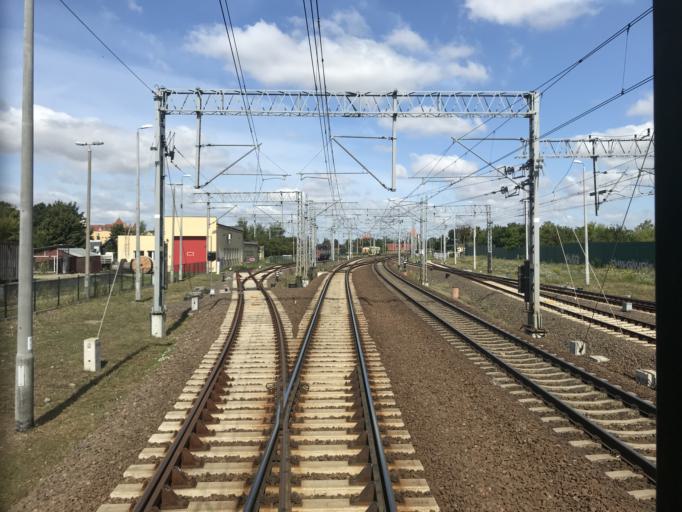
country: PL
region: Pomeranian Voivodeship
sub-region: Powiat malborski
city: Malbork
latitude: 54.0389
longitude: 19.0372
